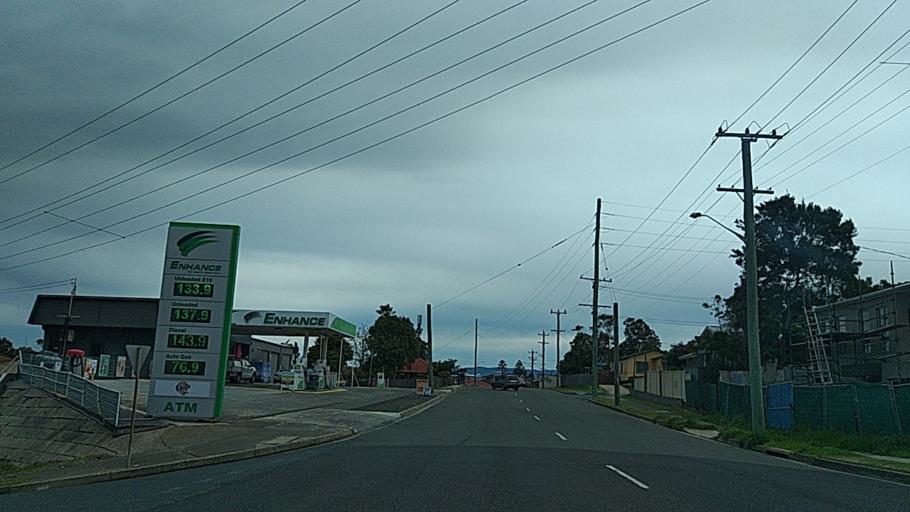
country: AU
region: New South Wales
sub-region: Wollongong
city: Port Kembla
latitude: -34.4851
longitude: 150.9037
